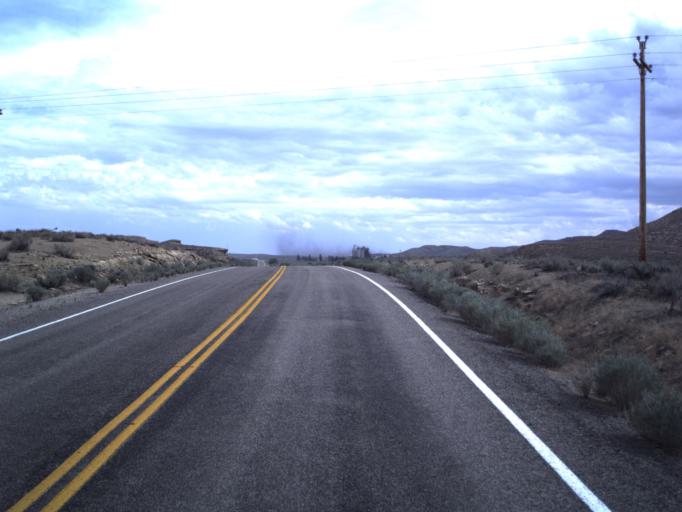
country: US
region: Colorado
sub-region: Rio Blanco County
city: Rangely
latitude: 40.0372
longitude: -109.1843
